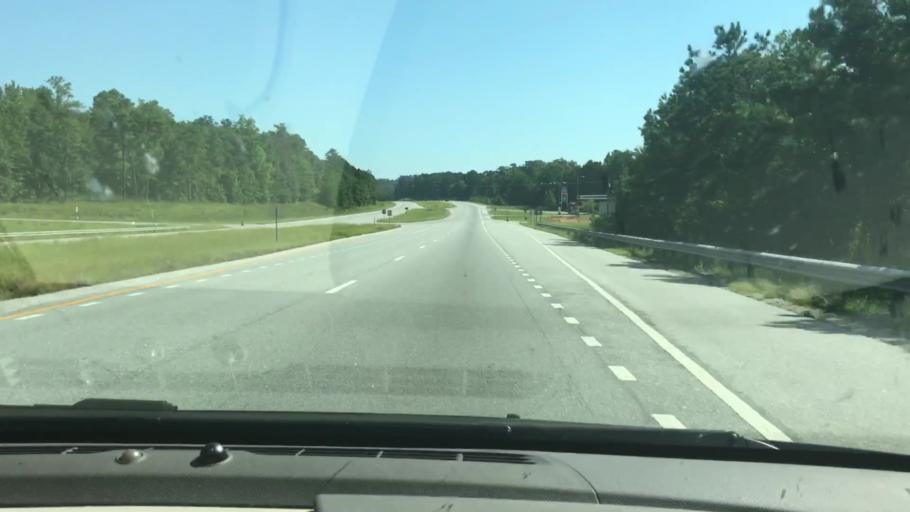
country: US
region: Alabama
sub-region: Russell County
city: Ladonia
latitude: 32.4019
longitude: -85.0593
